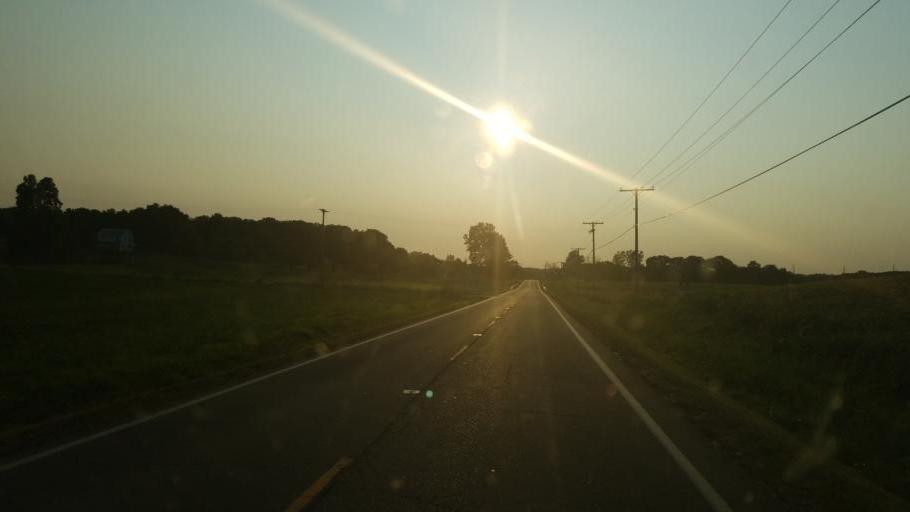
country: US
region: Ohio
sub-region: Wayne County
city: Shreve
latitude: 40.6683
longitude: -82.0760
